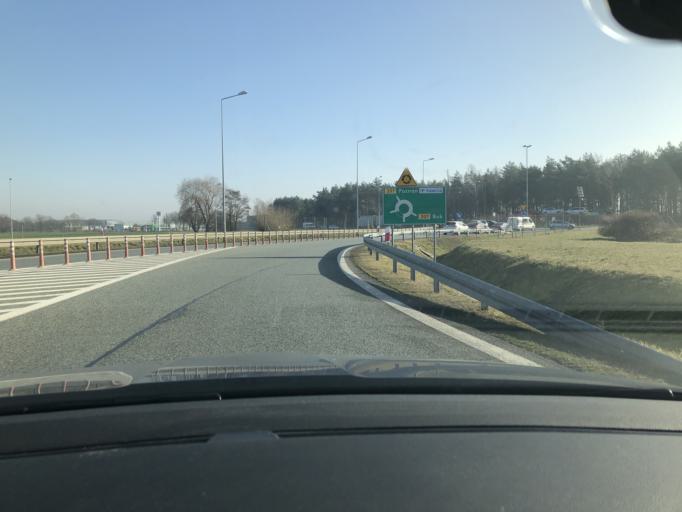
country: PL
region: Greater Poland Voivodeship
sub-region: Powiat poznanski
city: Buk
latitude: 52.3782
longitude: 16.5699
